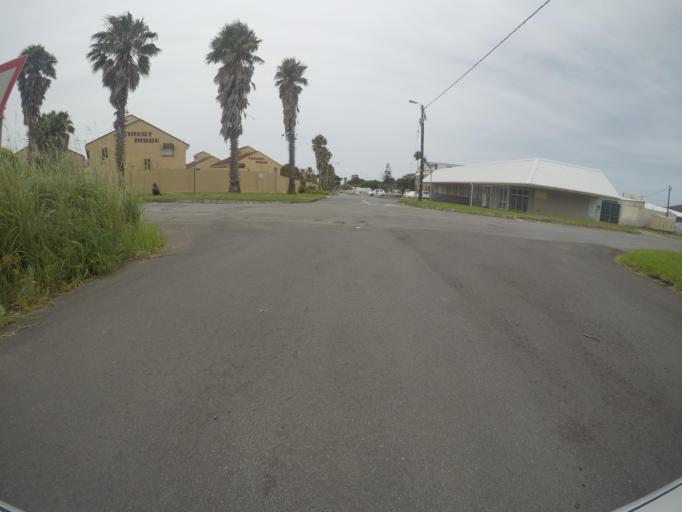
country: ZA
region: Eastern Cape
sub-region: Buffalo City Metropolitan Municipality
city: East London
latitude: -32.9630
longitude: 27.9327
